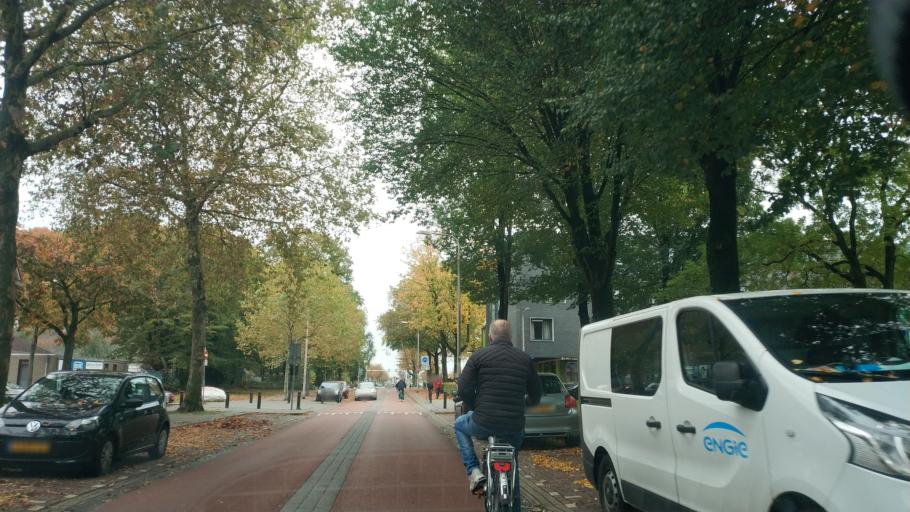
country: NL
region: North Brabant
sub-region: Gemeente Tilburg
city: Tilburg
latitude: 51.5463
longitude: 5.0776
